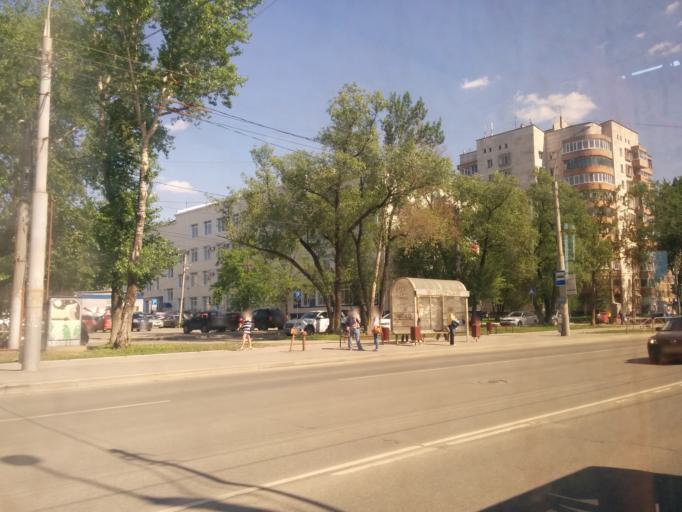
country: RU
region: Perm
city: Perm
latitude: 58.0109
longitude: 56.2805
